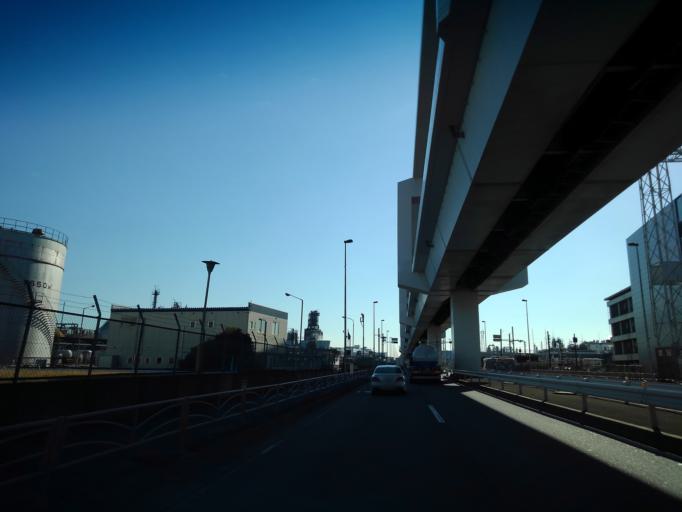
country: JP
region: Kanagawa
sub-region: Kawasaki-shi
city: Kawasaki
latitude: 35.5289
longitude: 139.7737
